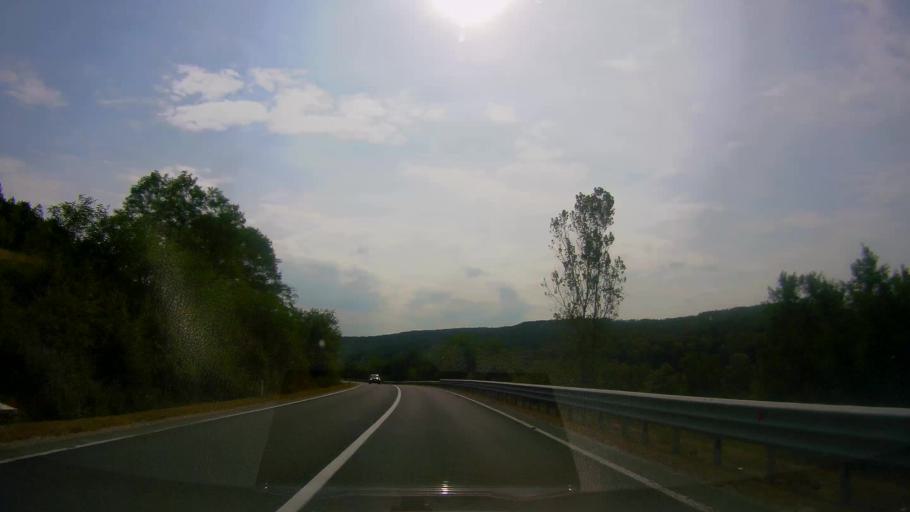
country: RO
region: Salaj
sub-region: Comuna Zimbor
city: Zimbor
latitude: 46.9747
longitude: 23.2555
